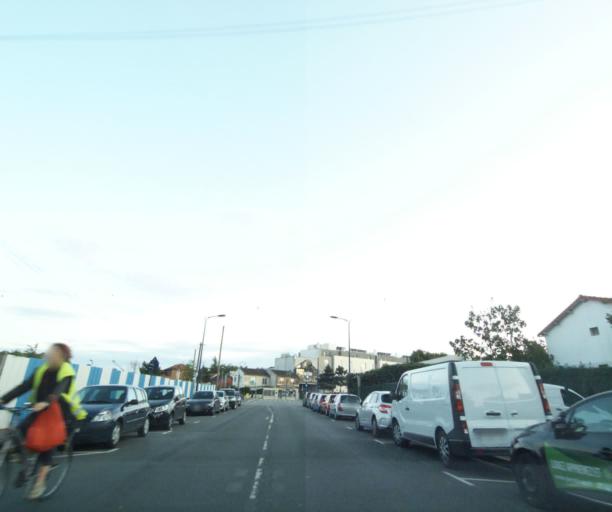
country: FR
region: Ile-de-France
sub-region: Departement des Hauts-de-Seine
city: Le Plessis-Robinson
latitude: 48.7910
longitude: 2.2628
